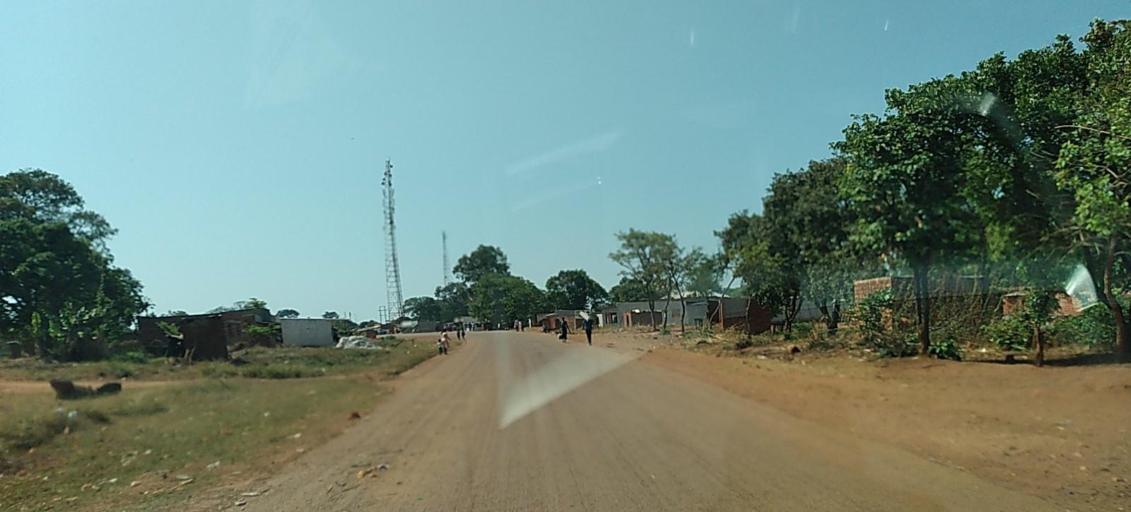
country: ZM
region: North-Western
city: Solwezi
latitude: -12.1068
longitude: 25.4950
